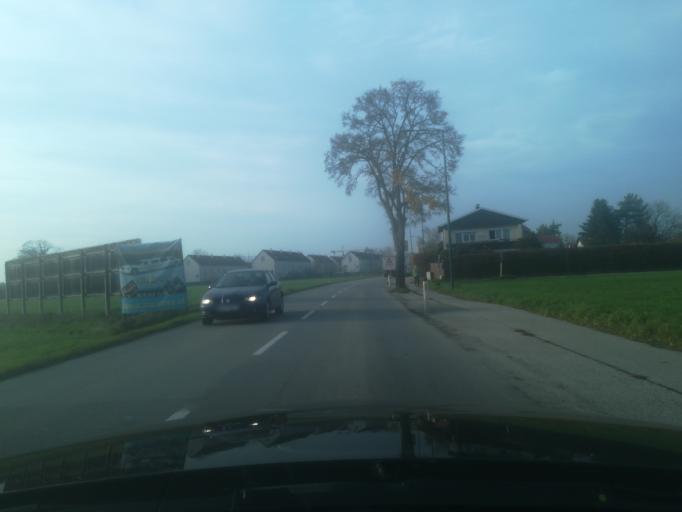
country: AT
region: Upper Austria
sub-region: Wels Stadt
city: Wels
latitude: 48.1670
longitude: 14.0006
